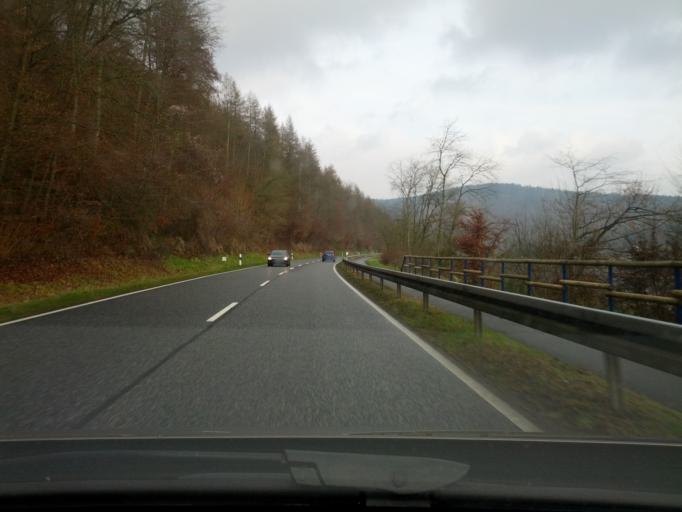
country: DE
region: Lower Saxony
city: Bad Karlshafen
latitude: 51.6414
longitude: 9.4912
